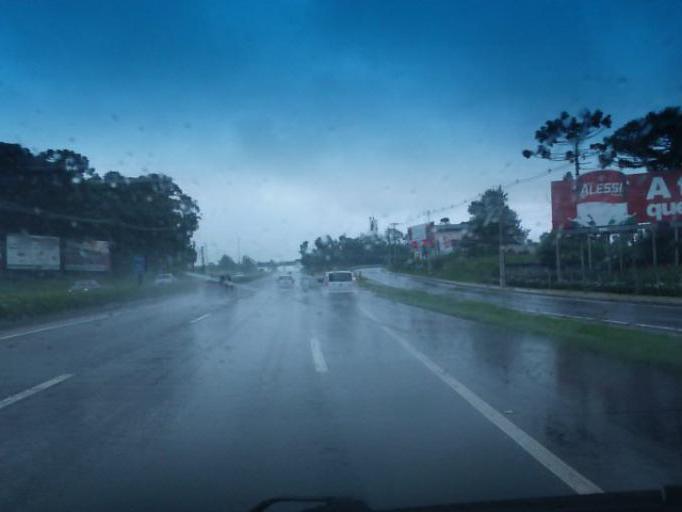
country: BR
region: Parana
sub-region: Sao Jose Dos Pinhais
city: Sao Jose dos Pinhais
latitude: -25.5739
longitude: -49.1800
